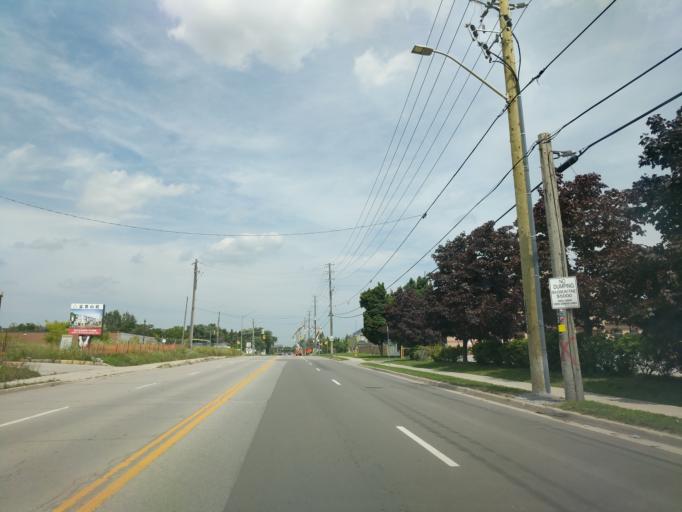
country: CA
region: Ontario
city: Markham
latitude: 43.8283
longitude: -79.3009
